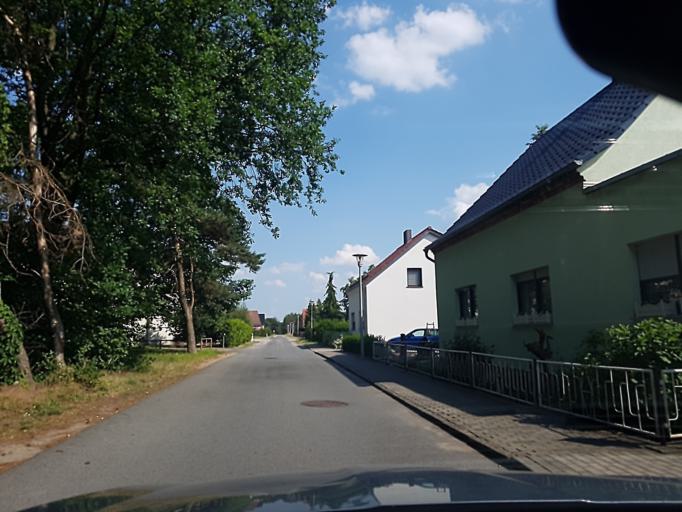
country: DE
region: Brandenburg
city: Ruckersdorf
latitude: 51.5625
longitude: 13.5557
